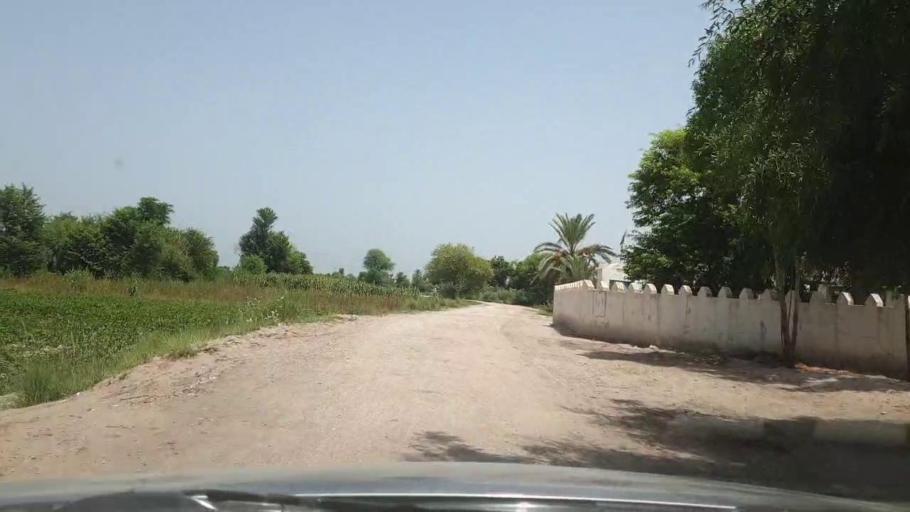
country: PK
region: Sindh
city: Pano Aqil
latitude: 27.8298
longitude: 69.2102
